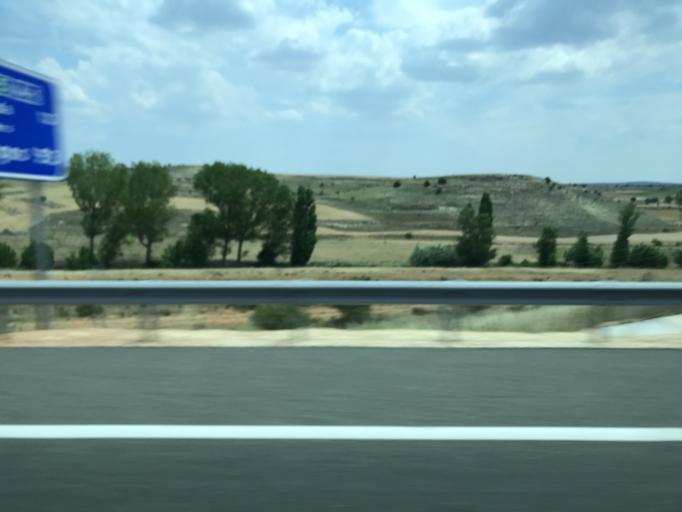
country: ES
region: Castille and Leon
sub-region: Provincia de Burgos
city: Pardilla
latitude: 41.5585
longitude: -3.7112
